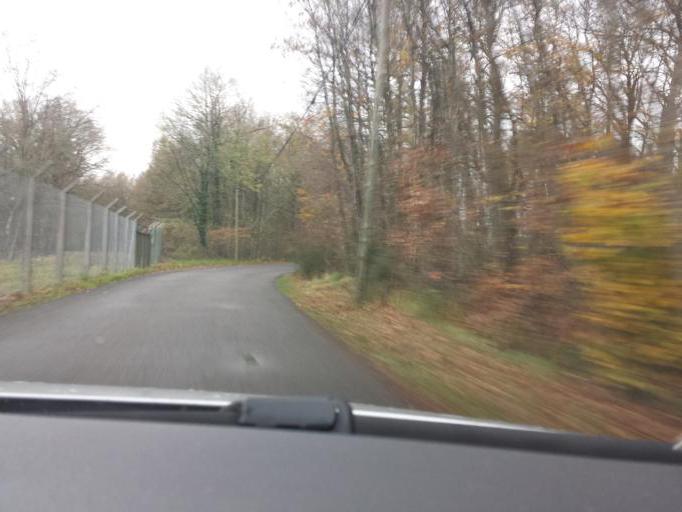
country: FR
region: Haute-Normandie
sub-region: Departement de l'Eure
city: Evreux
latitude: 48.9949
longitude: 1.2178
